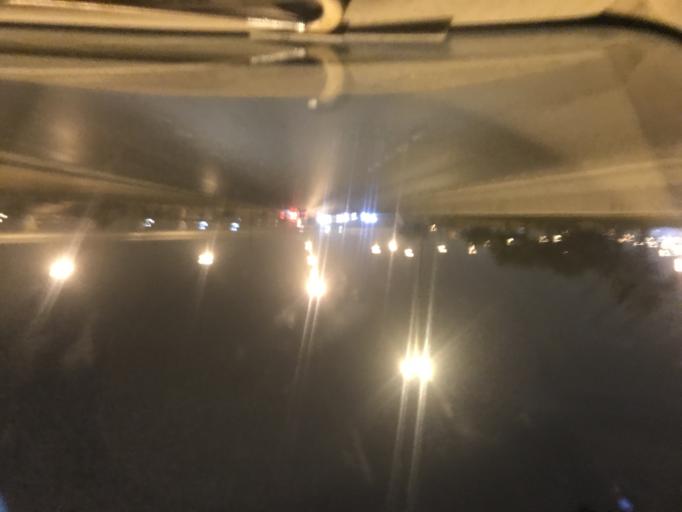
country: SA
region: Ar Riyad
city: Riyadh
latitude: 24.8277
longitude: 46.7226
